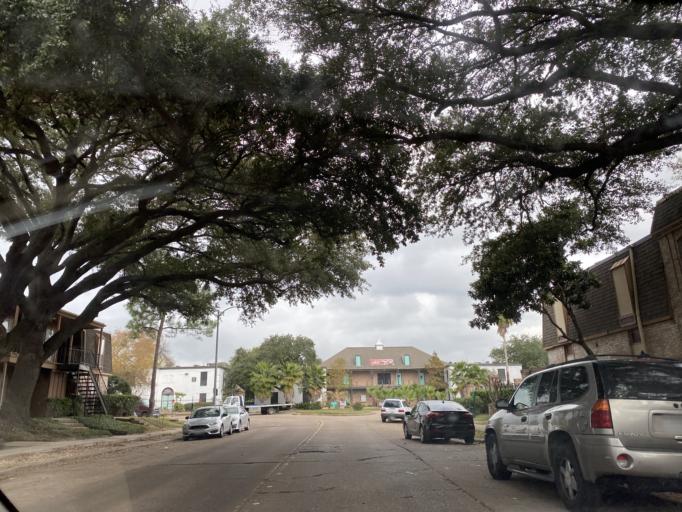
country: US
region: Texas
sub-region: Harris County
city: Piney Point Village
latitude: 29.7419
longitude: -95.4966
